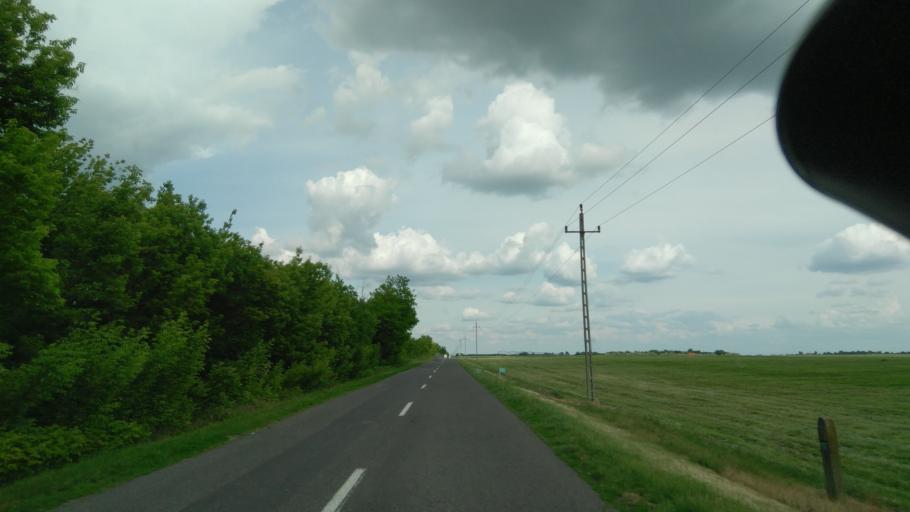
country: HU
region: Bekes
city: Mezohegyes
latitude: 46.3096
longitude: 20.8714
